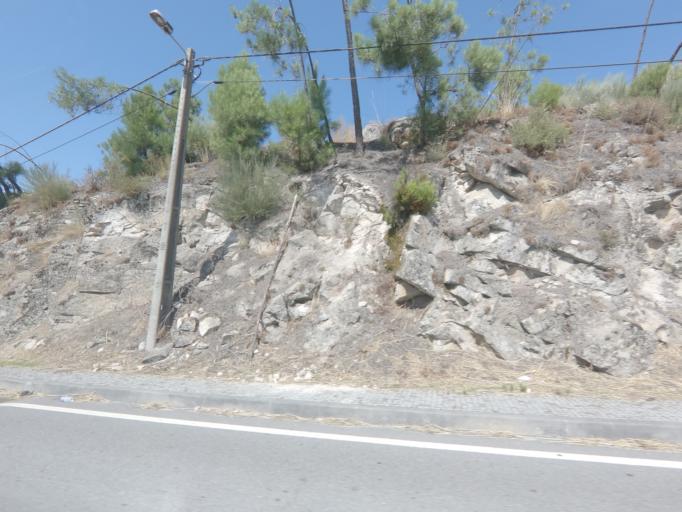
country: PT
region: Viseu
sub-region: Tarouca
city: Tarouca
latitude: 41.0257
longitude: -7.7544
